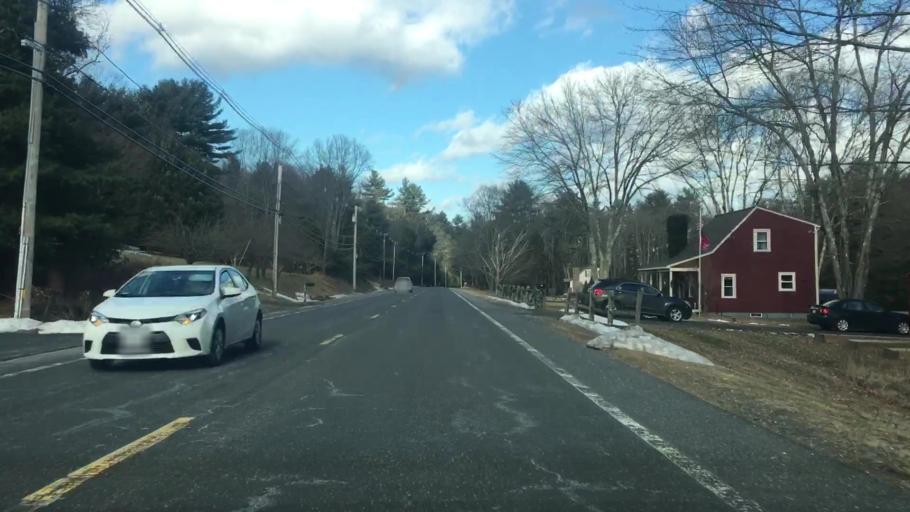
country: US
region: Massachusetts
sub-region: Hampden County
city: Brimfield
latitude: 42.0948
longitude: -72.2014
